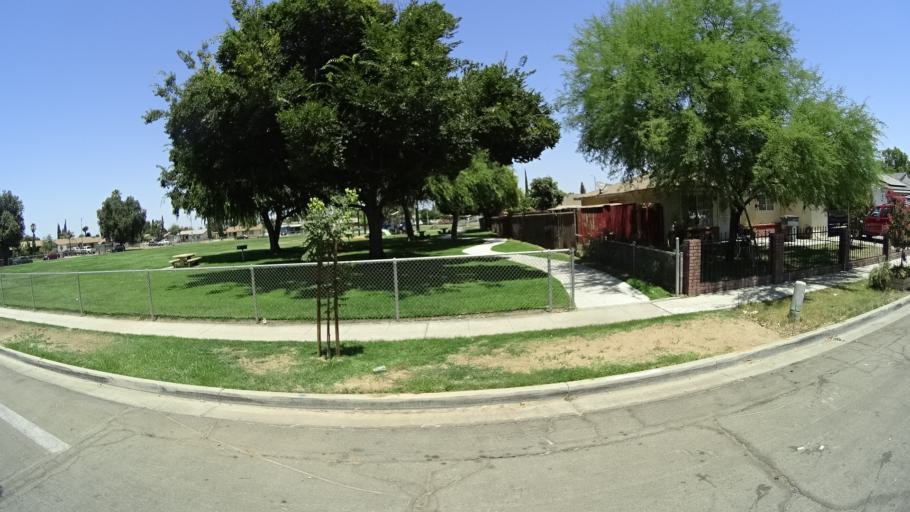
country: US
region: California
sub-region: Fresno County
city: West Park
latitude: 36.7301
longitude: -119.8309
